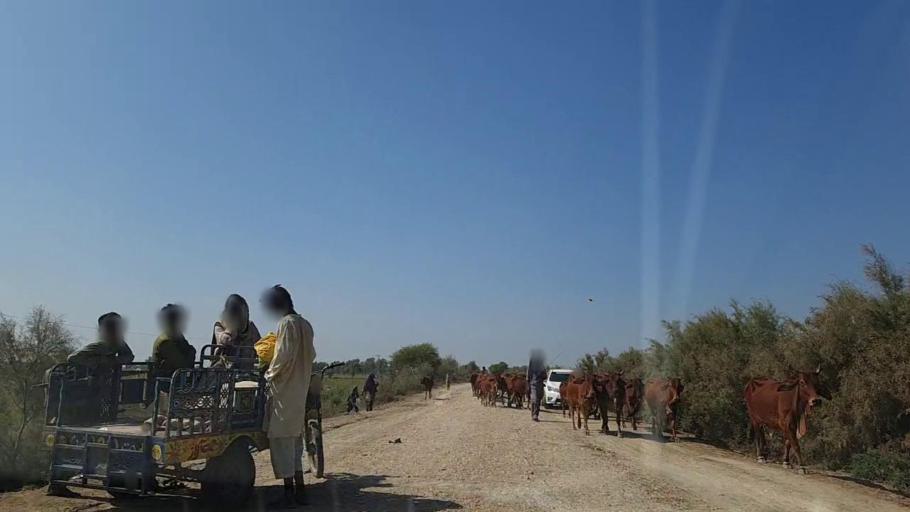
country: PK
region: Sindh
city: Chuhar Jamali
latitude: 24.4184
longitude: 68.0218
